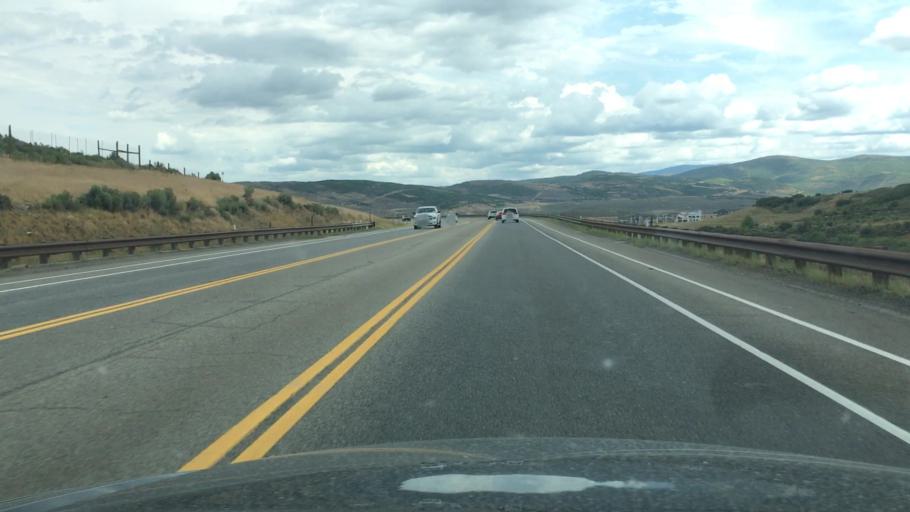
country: US
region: Utah
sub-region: Summit County
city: Park City
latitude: 40.6720
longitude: -111.4738
